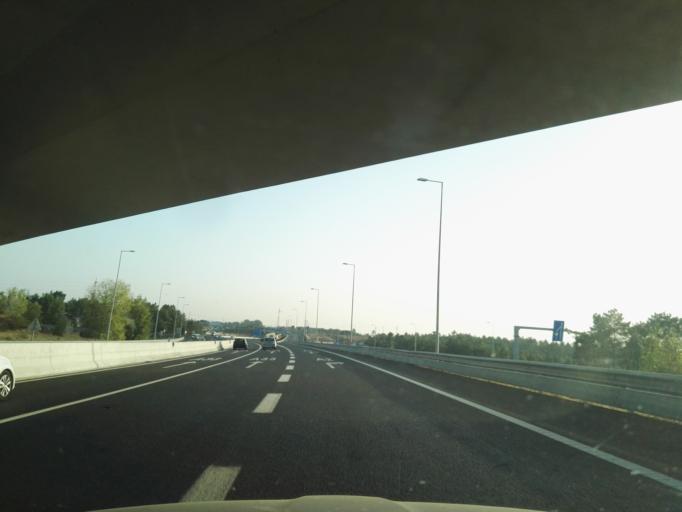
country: PT
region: Setubal
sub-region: Barreiro
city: Santo Antonio da Charneca
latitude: 38.6044
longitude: -9.0203
